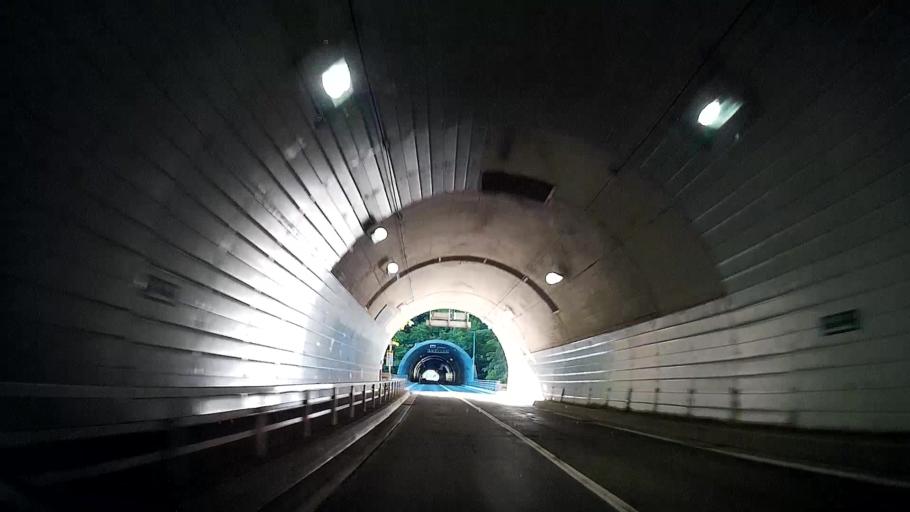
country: JP
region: Hokkaido
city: Sapporo
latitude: 42.9953
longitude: 141.1580
